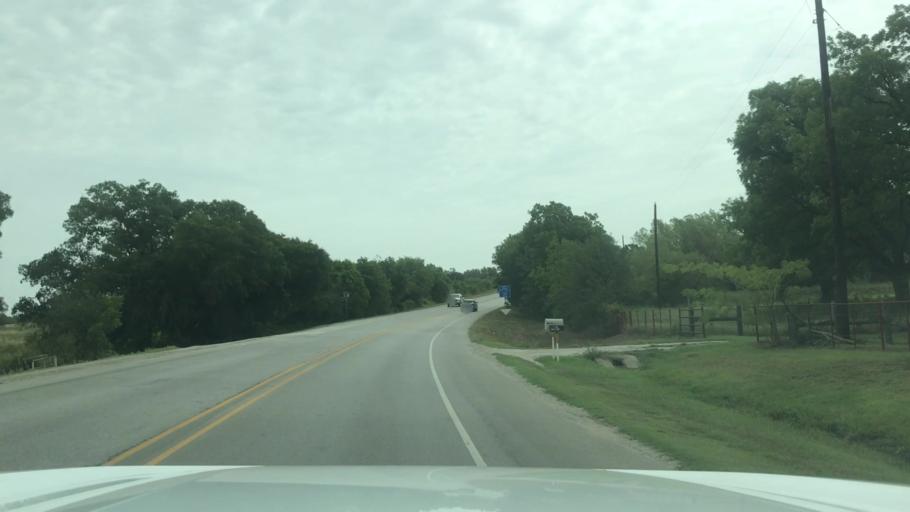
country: US
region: Texas
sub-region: Erath County
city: Dublin
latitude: 32.0986
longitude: -98.3978
